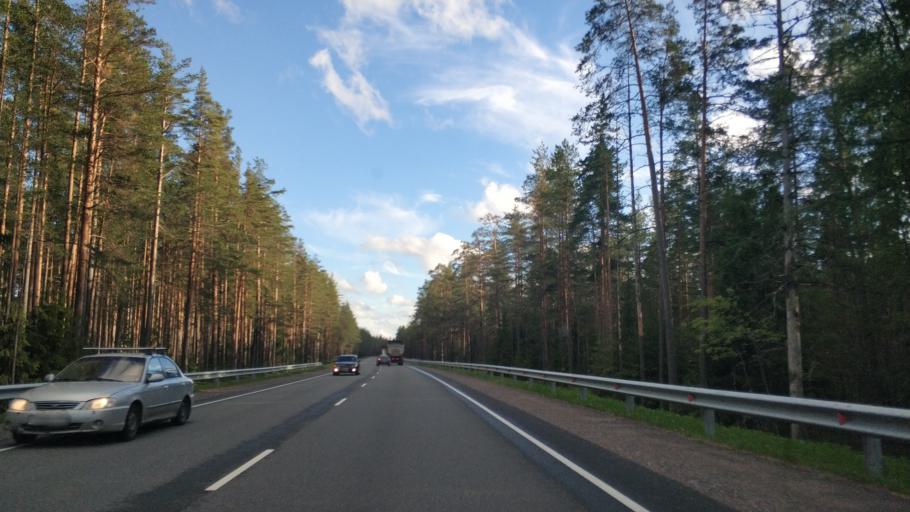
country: RU
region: Leningrad
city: Priozersk
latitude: 60.8910
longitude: 30.1597
